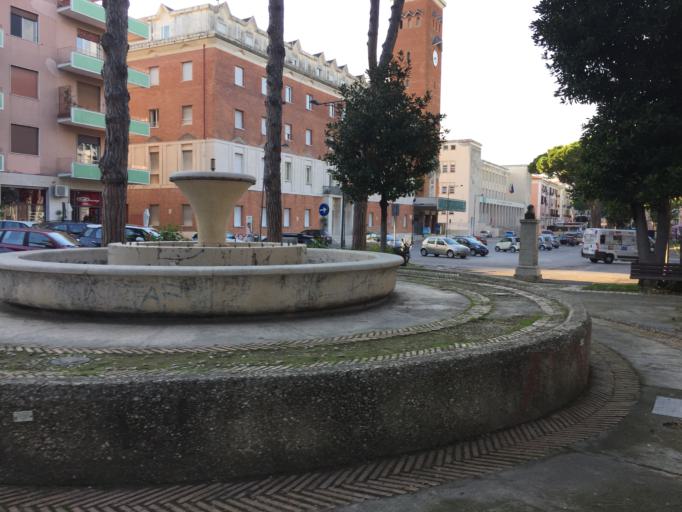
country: IT
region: Latium
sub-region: Provincia di Latina
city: Gaeta
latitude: 41.2133
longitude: 13.5725
